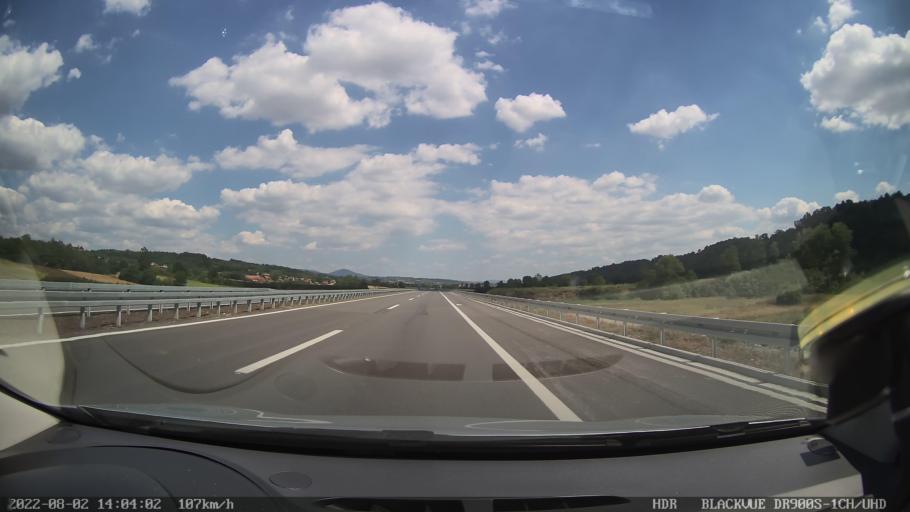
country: RS
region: Central Serbia
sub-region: Moravicki Okrug
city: Cacak
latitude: 43.9239
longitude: 20.3627
